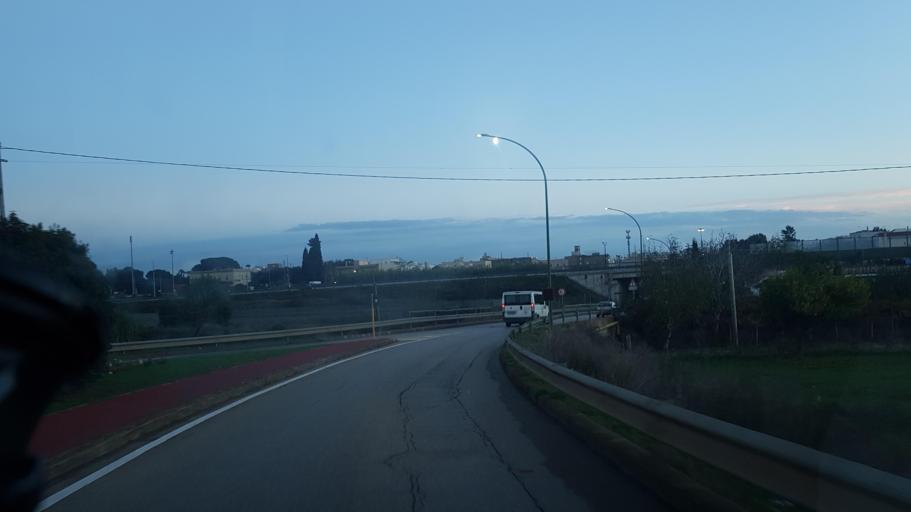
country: IT
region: Apulia
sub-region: Provincia di Brindisi
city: Latiano
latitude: 40.5598
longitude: 17.7148
